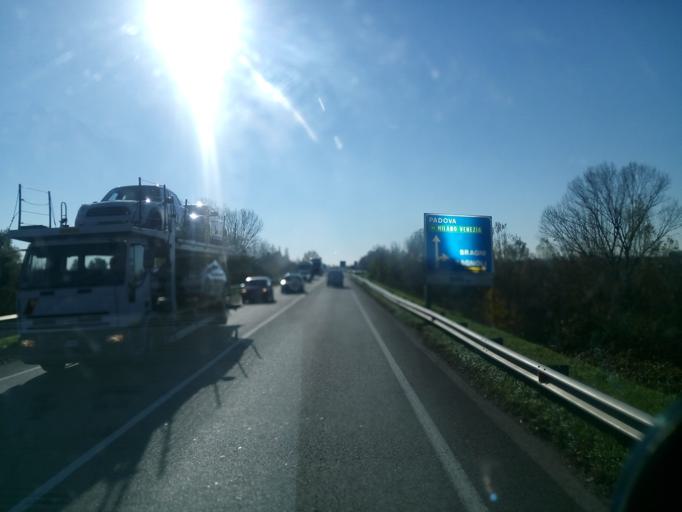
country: IT
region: Veneto
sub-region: Provincia di Padova
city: Mejaniga
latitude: 45.4742
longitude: 11.9197
